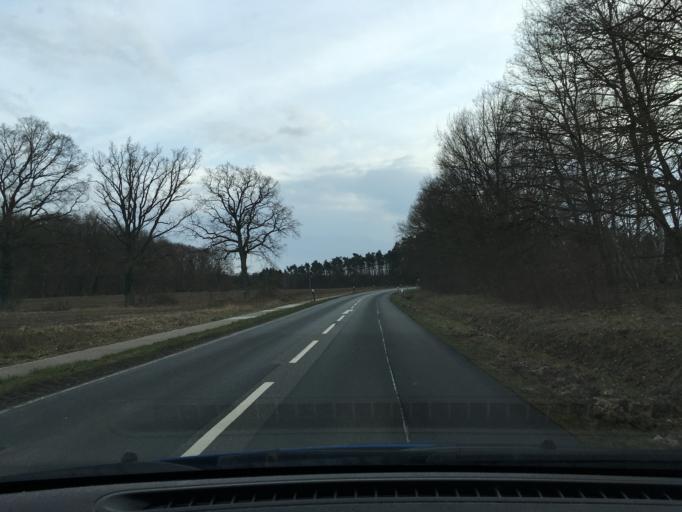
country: DE
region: Lower Saxony
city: Reppenstedt
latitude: 53.2634
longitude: 10.3400
